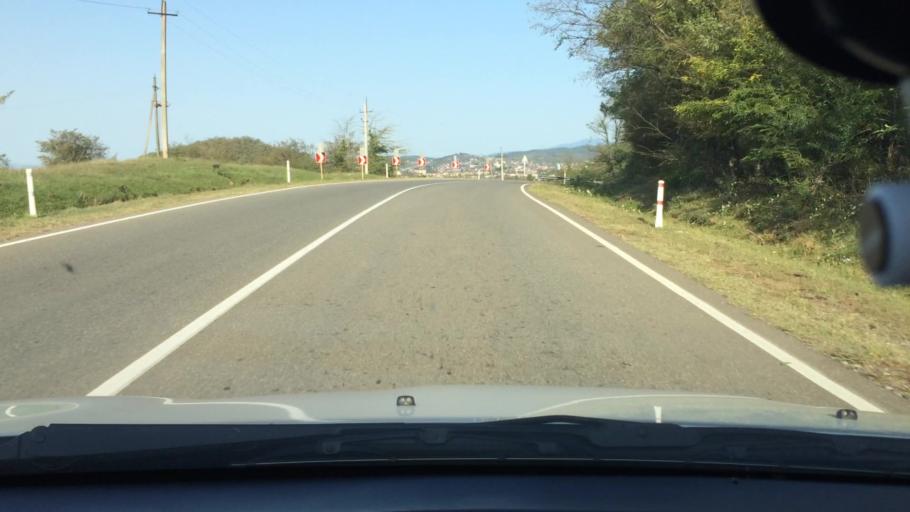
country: GE
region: Imereti
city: Kutaisi
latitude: 42.2519
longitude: 42.7506
